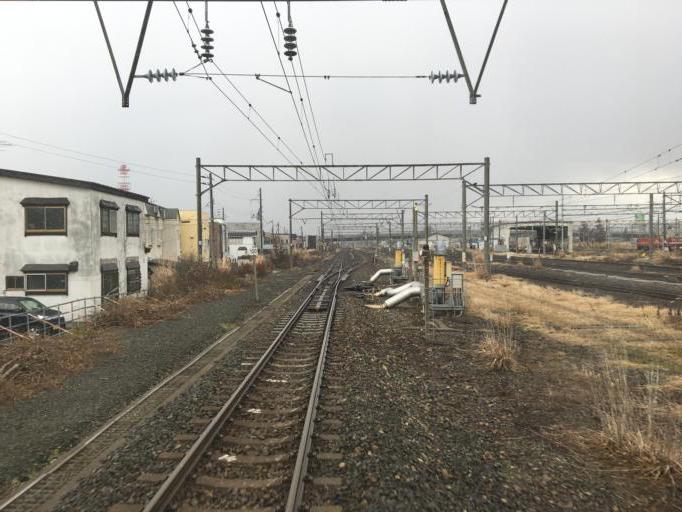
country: JP
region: Aomori
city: Aomori Shi
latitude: 40.8188
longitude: 140.7385
